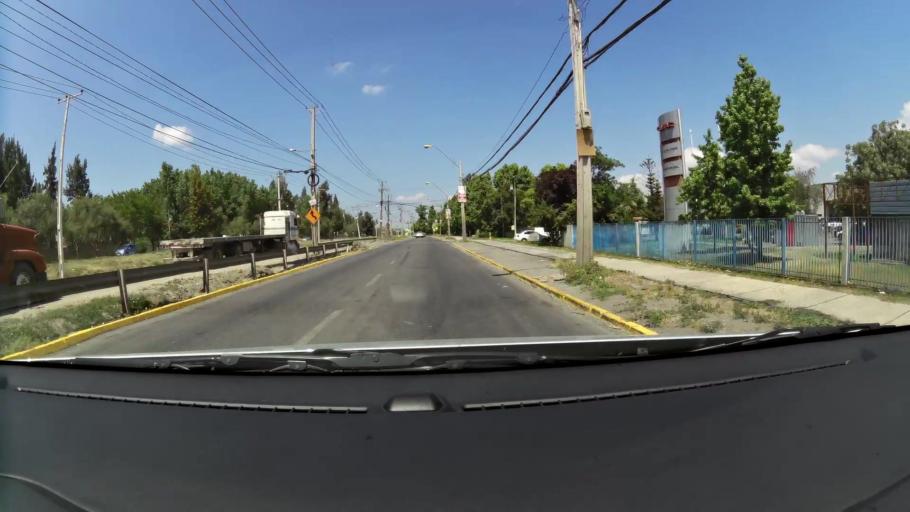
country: CL
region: Santiago Metropolitan
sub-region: Provincia de Maipo
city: San Bernardo
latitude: -33.5302
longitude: -70.7316
